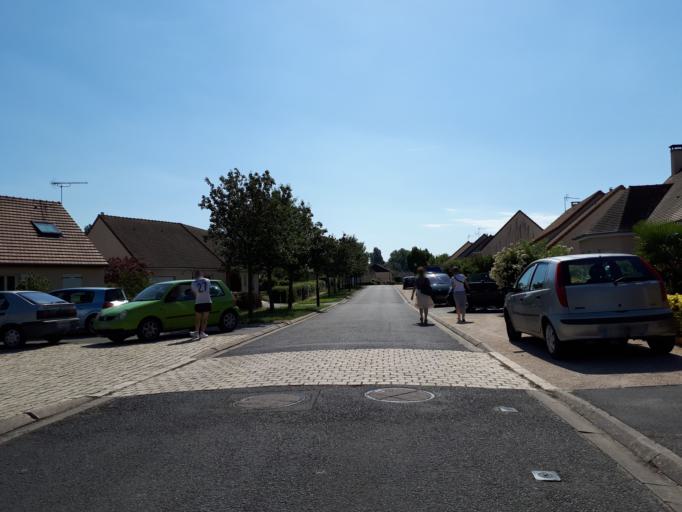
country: FR
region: Pays de la Loire
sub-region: Departement de la Sarthe
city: Champagne
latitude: 48.0768
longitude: 0.2913
